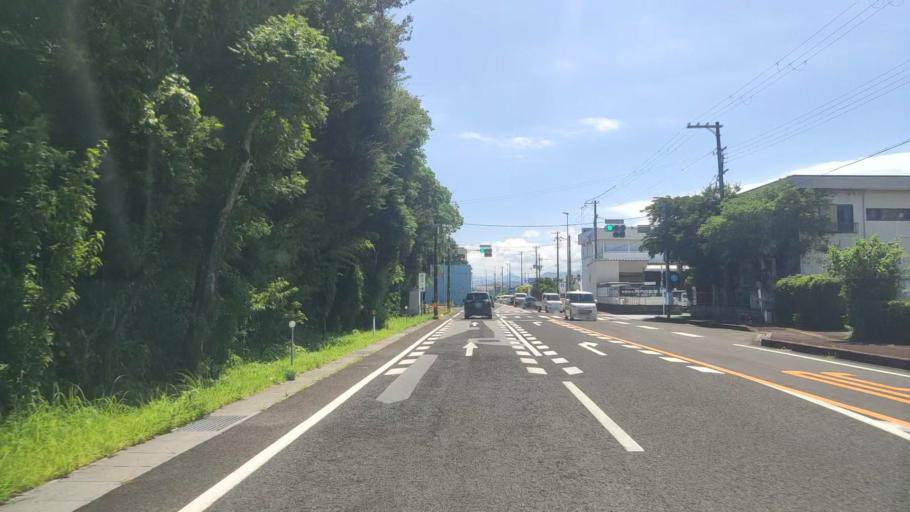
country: JP
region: Wakayama
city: Shingu
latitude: 33.8752
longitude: 136.0888
